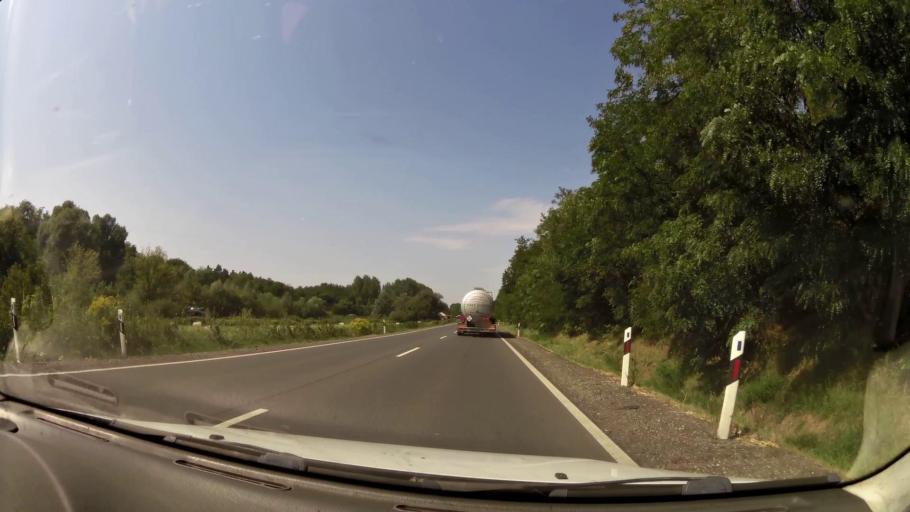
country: HU
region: Pest
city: Mende
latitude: 47.4267
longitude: 19.4312
